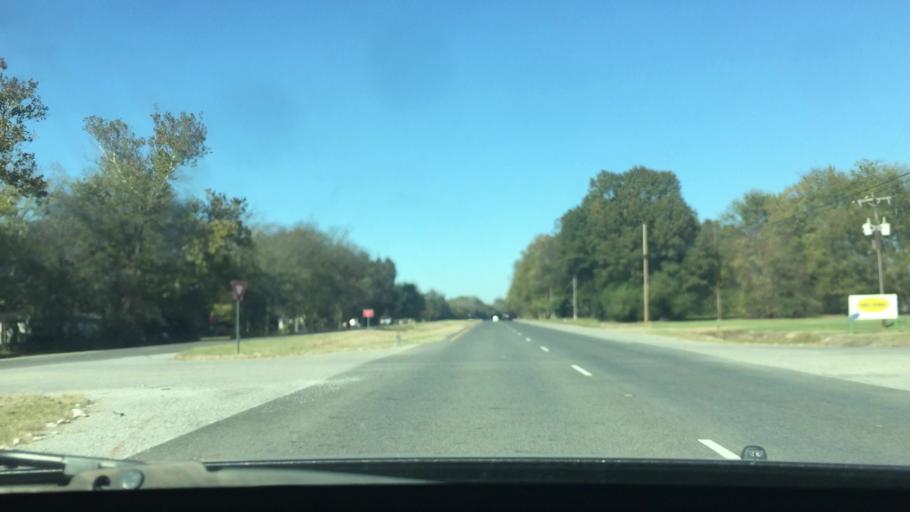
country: US
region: Louisiana
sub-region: Richland Parish
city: Rayville
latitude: 32.3923
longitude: -91.7694
